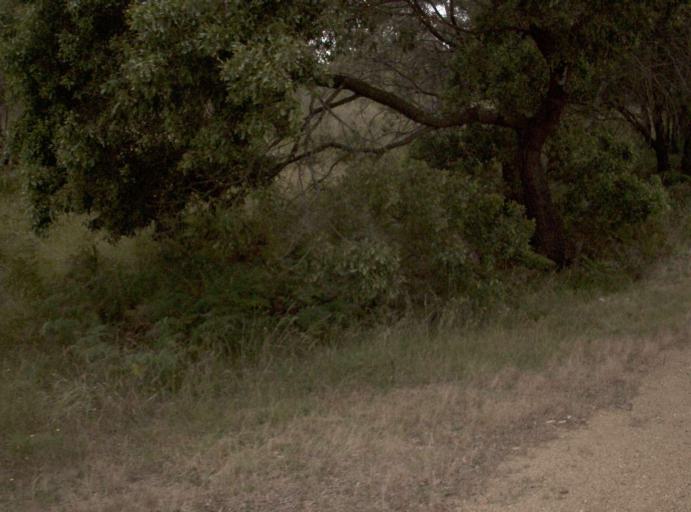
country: AU
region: Victoria
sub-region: Wellington
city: Sale
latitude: -38.0016
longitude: 147.3051
